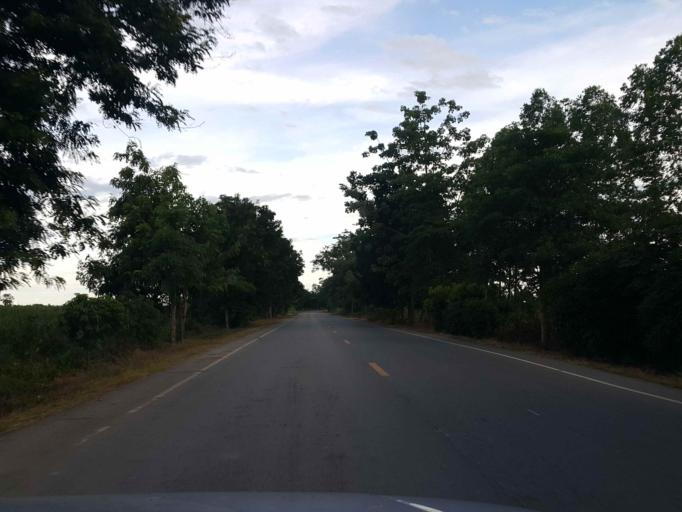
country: TH
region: Sukhothai
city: Sawankhalok
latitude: 17.3747
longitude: 99.7398
